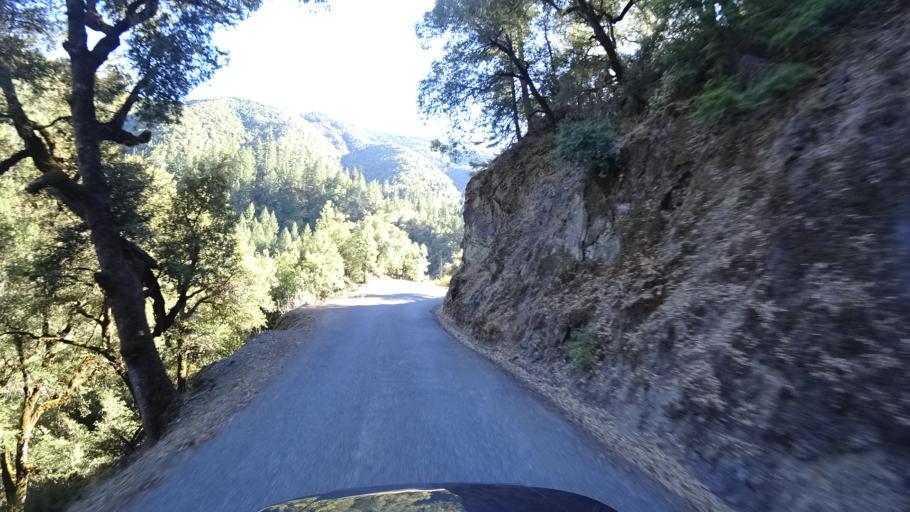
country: US
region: California
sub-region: Humboldt County
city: Willow Creek
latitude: 41.2745
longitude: -123.2812
